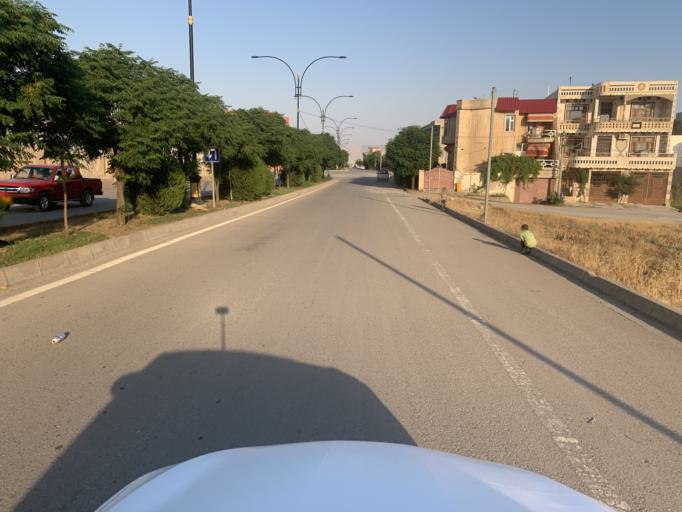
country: IQ
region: As Sulaymaniyah
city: Raniye
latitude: 36.2402
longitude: 44.8761
